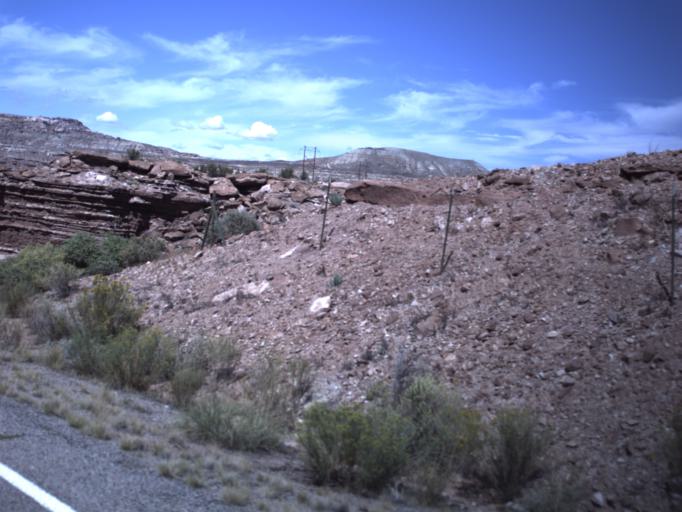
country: US
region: Utah
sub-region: San Juan County
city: Blanding
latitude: 37.2900
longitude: -109.3998
